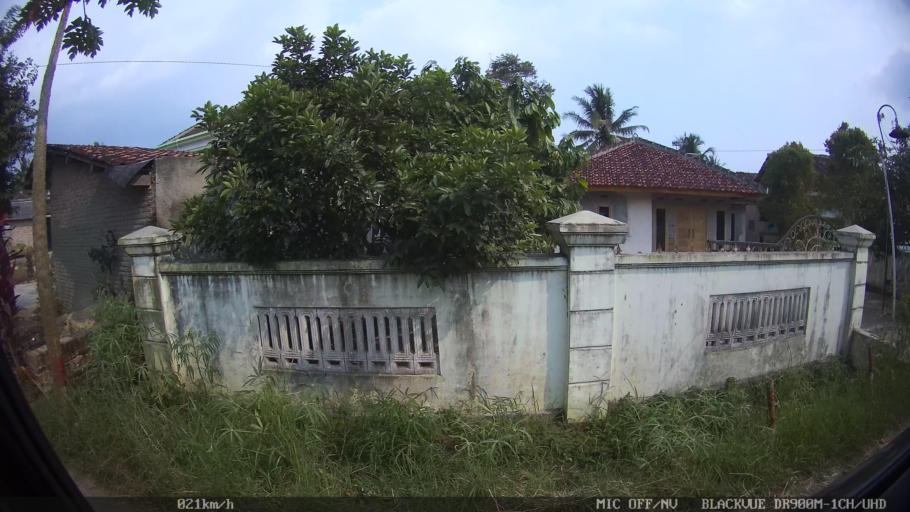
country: ID
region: Lampung
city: Gadingrejo
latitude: -5.4065
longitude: 105.0231
